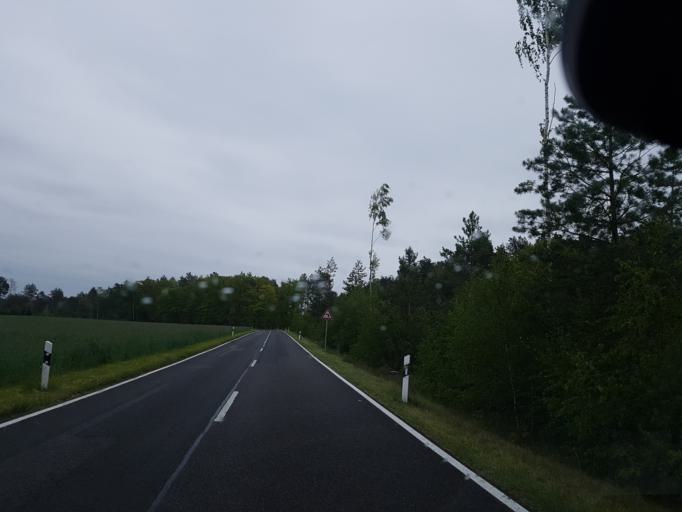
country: DE
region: Brandenburg
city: Drebkau
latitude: 51.6531
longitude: 14.2856
